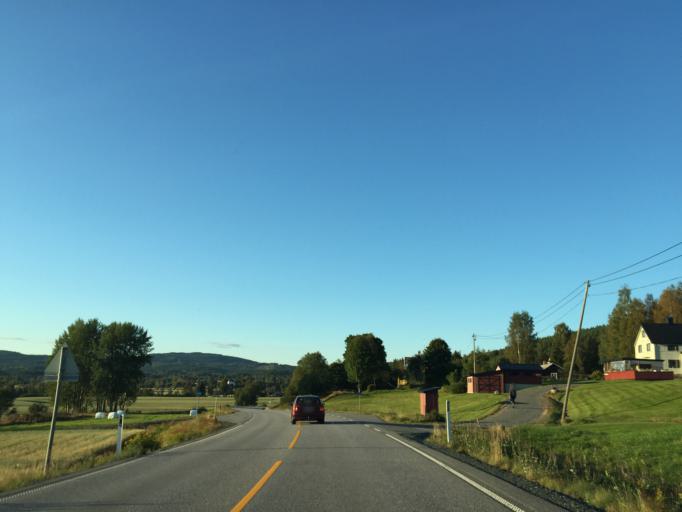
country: NO
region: Hedmark
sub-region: Nord-Odal
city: Sand
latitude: 60.4206
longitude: 11.5133
